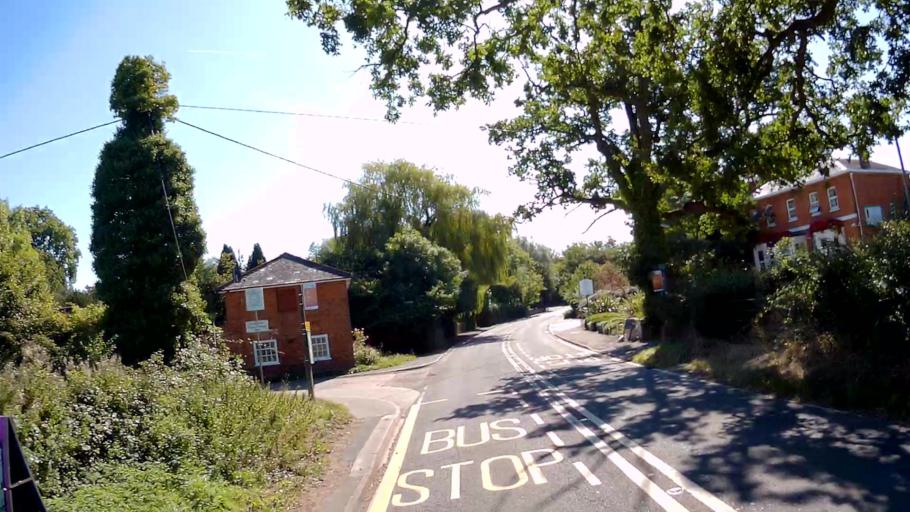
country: GB
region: England
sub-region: Wokingham
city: Swallowfield
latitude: 51.3829
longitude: -0.9666
